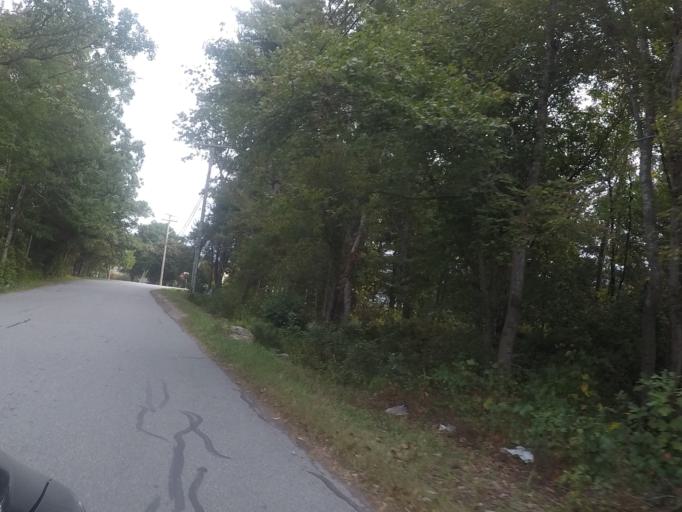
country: US
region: Massachusetts
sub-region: Bristol County
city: Head of Westport
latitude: 41.6617
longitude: -71.0373
